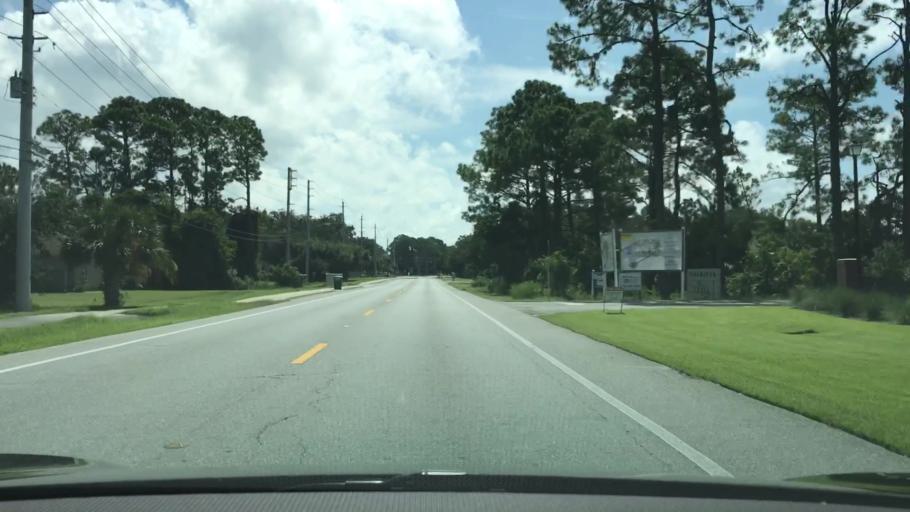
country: US
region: Florida
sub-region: Bay County
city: Lower Grand Lagoon
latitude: 30.1580
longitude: -85.7596
